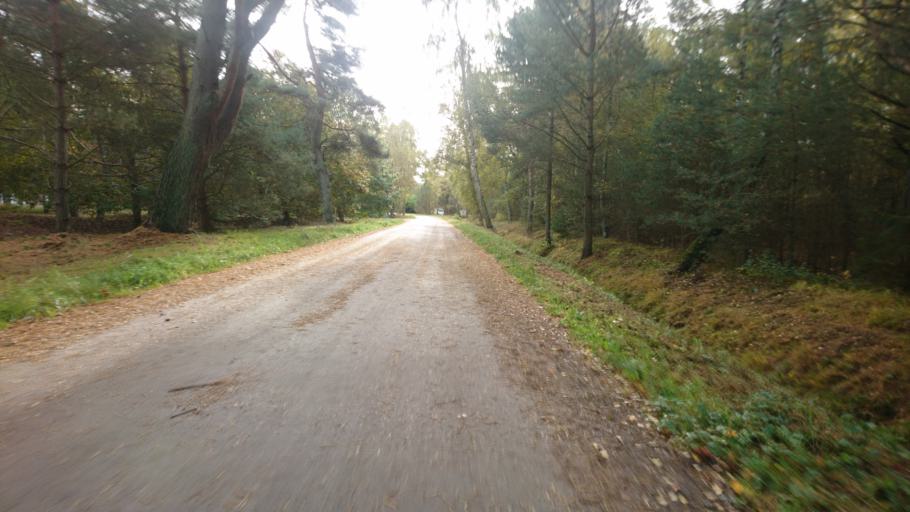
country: SE
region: Skane
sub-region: Vellinge Kommun
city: Ljunghusen
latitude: 55.3988
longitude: 12.9115
